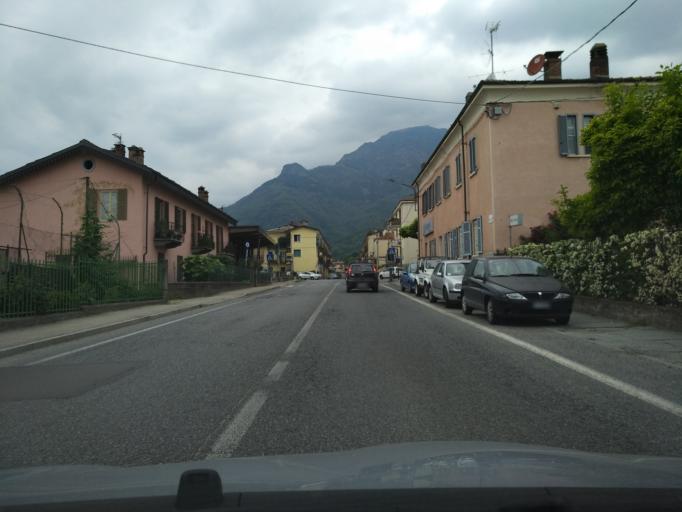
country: IT
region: Piedmont
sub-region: Provincia di Torino
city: Torre Pellice
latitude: 44.8203
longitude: 7.2311
